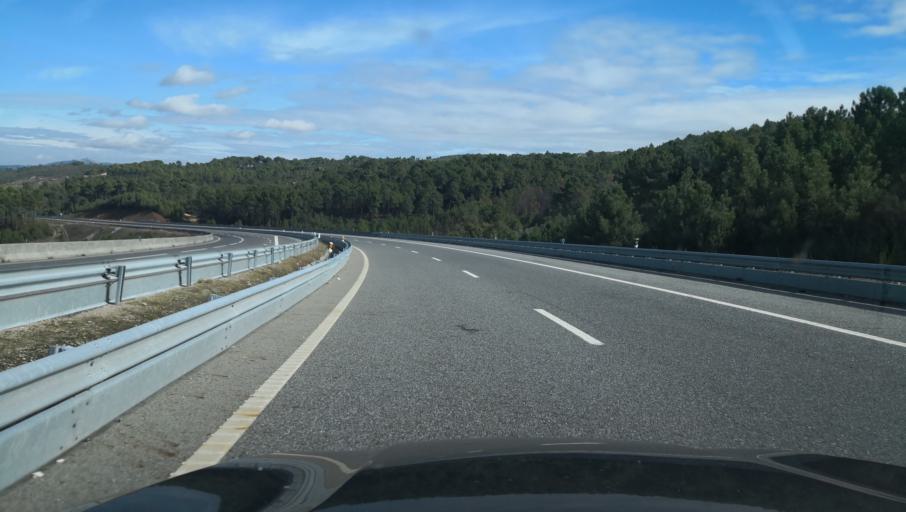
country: PT
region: Vila Real
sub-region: Boticas
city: Boticas
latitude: 41.6160
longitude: -7.6097
